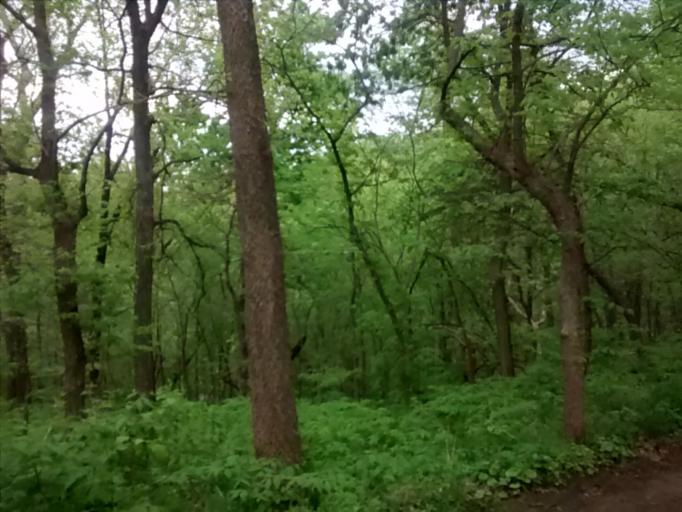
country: US
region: Nebraska
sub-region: Sarpy County
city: Bellevue
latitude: 41.1823
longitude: -95.9057
